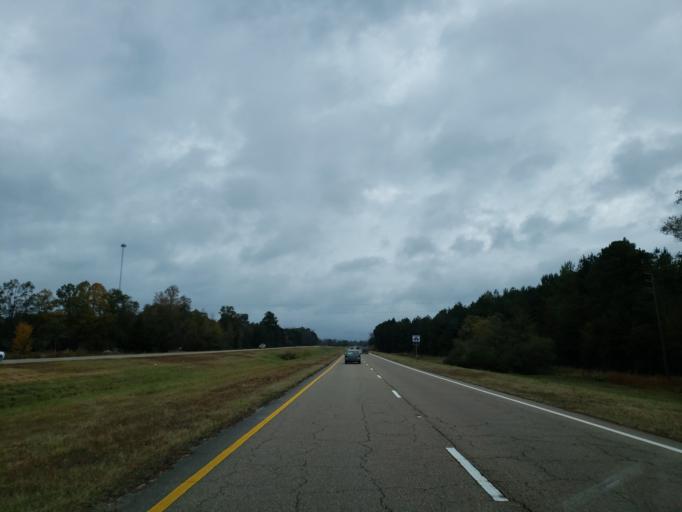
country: US
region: Mississippi
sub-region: Clarke County
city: Quitman
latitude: 31.9365
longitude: -88.7174
